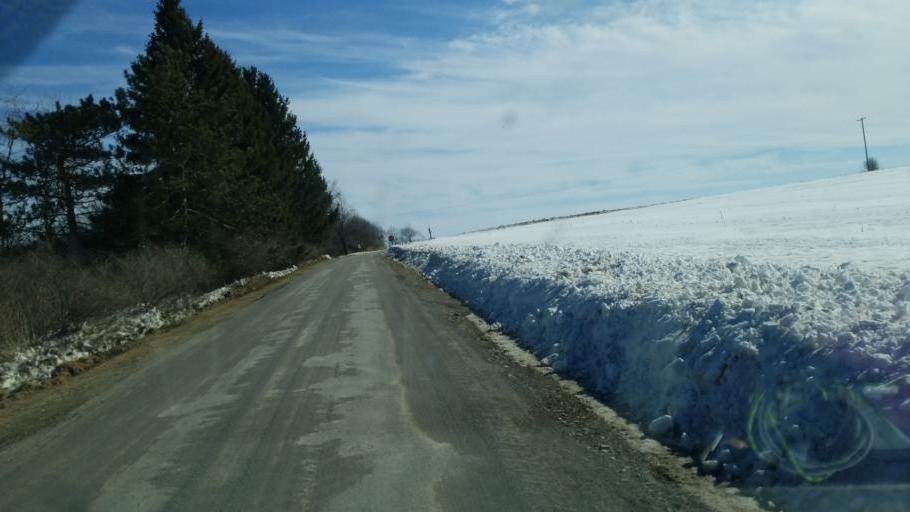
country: US
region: New York
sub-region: Allegany County
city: Andover
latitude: 42.1195
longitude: -77.7597
